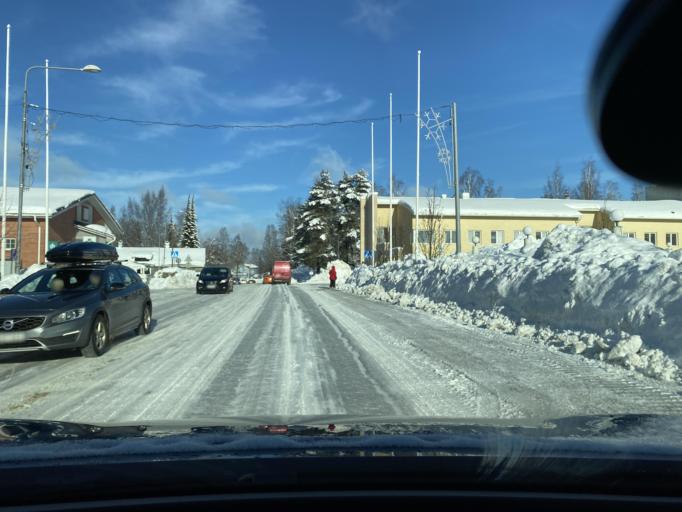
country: FI
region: Southern Savonia
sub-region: Mikkeli
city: Kangasniemi
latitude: 61.9895
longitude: 26.6435
